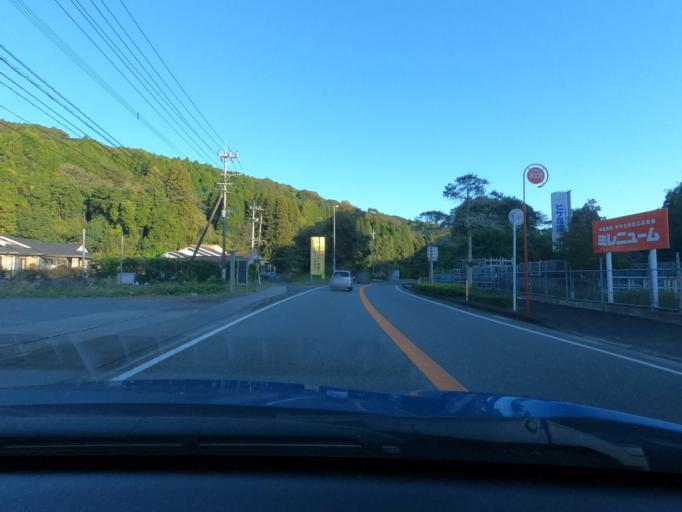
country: JP
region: Kagoshima
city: Satsumasendai
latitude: 31.8509
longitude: 130.2661
